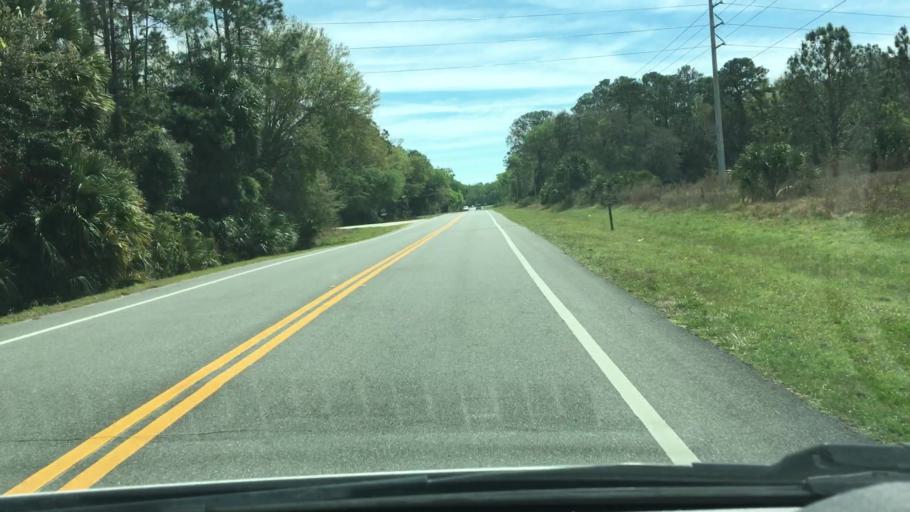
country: US
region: Florida
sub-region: Lake County
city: Lake Mack-Forest Hills
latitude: 29.0095
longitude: -81.3923
